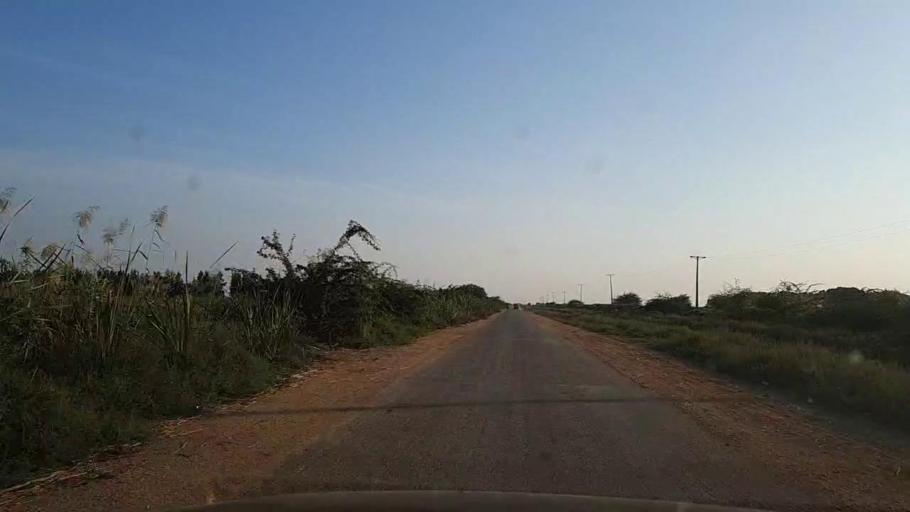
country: PK
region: Sindh
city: Thatta
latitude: 24.6451
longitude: 67.9124
